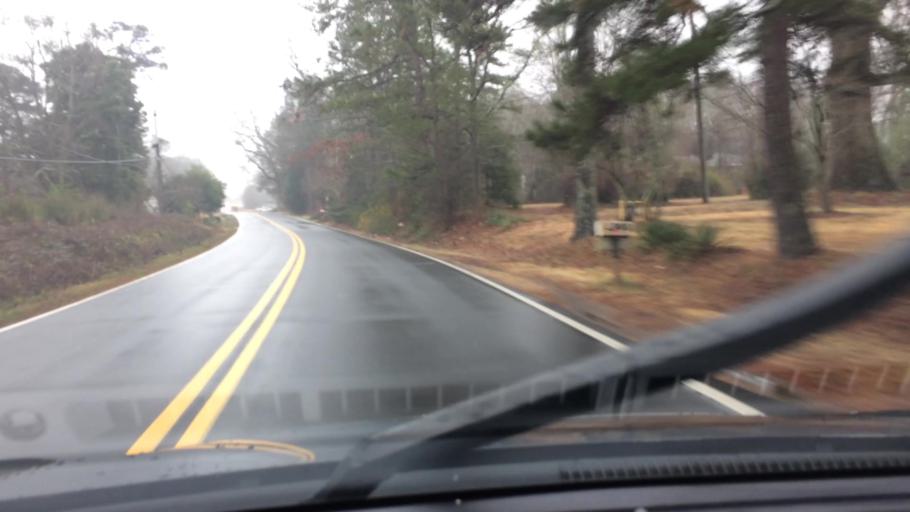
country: US
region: South Carolina
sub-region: Anderson County
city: Williamston
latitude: 34.6375
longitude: -82.4809
